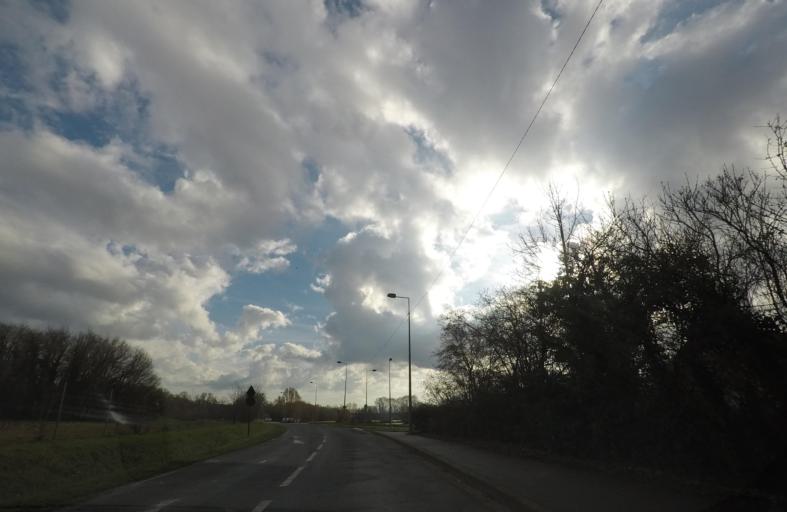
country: FR
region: Centre
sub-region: Departement du Cher
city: Bourges
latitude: 47.0510
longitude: 2.4068
